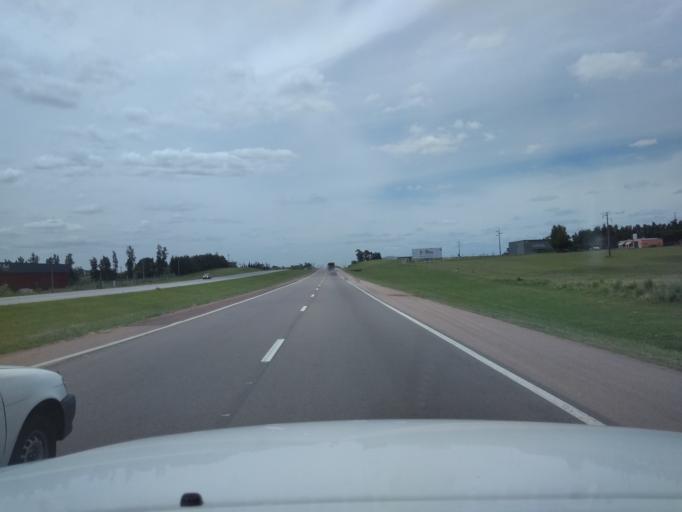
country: UY
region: Canelones
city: Las Piedras
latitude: -34.7358
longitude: -56.2499
